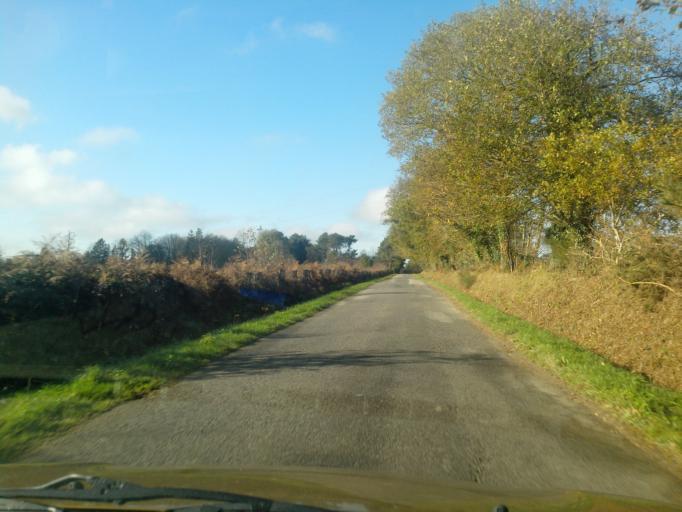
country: FR
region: Brittany
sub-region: Departement du Morbihan
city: Pleucadeuc
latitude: 47.7269
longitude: -2.3864
